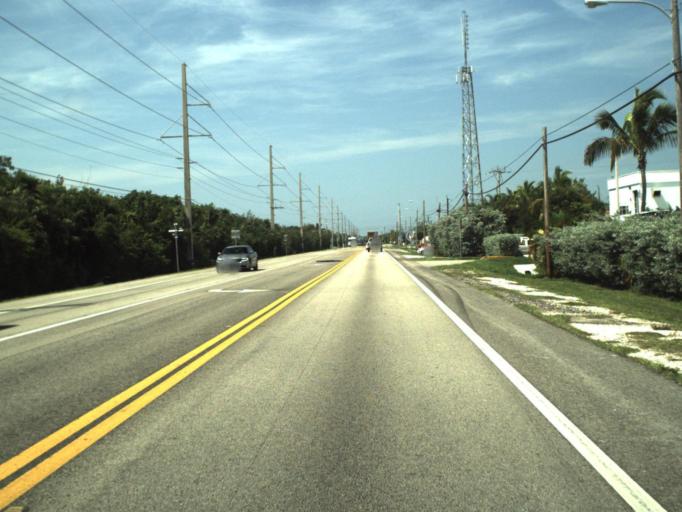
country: US
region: Florida
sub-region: Monroe County
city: Marathon
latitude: 24.7692
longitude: -80.9419
